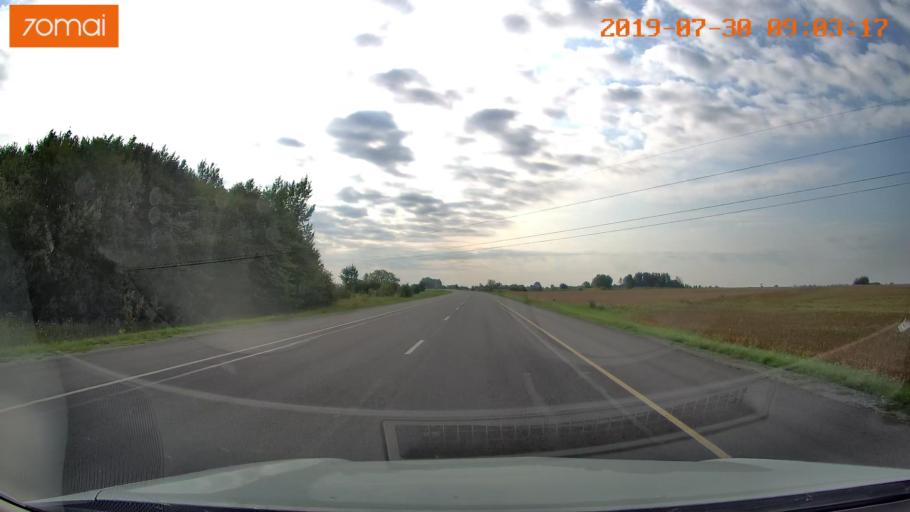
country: RU
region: Kaliningrad
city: Gusev
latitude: 54.6092
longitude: 22.2494
